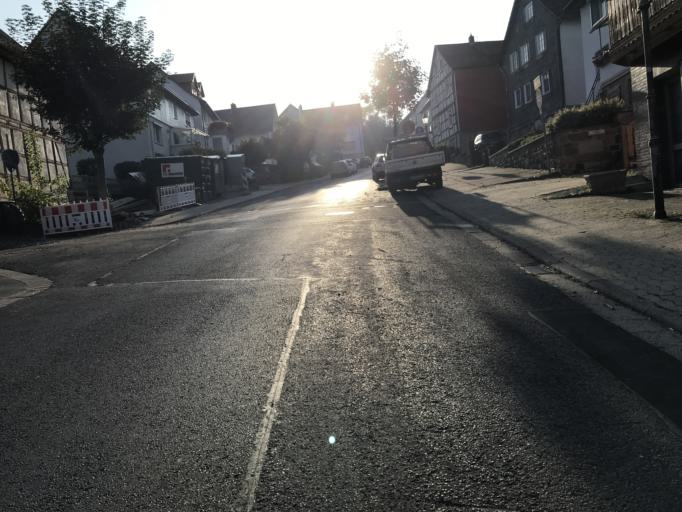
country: DE
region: Hesse
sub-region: Regierungsbezirk Kassel
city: Guxhagen
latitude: 51.2008
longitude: 9.4813
